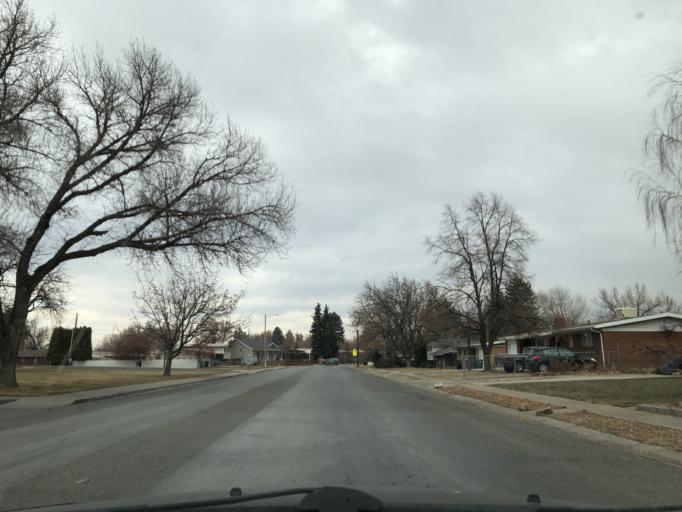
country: US
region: Utah
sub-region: Cache County
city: Logan
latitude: 41.7429
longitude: -111.8373
